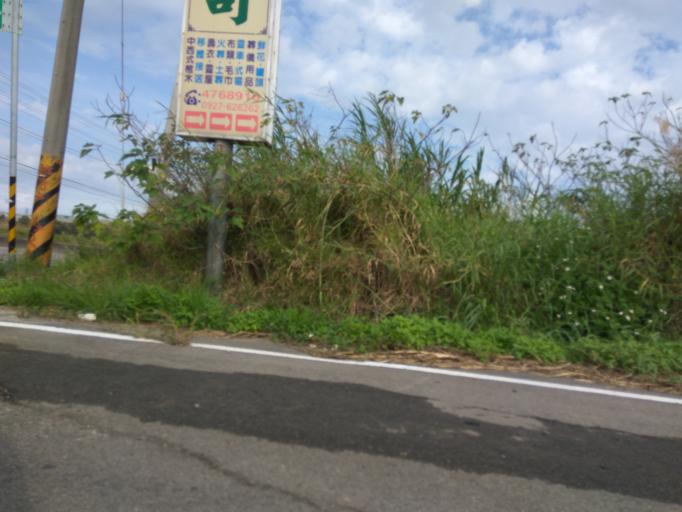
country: TW
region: Taiwan
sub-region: Hsinchu
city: Zhubei
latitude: 24.9781
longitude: 121.0270
